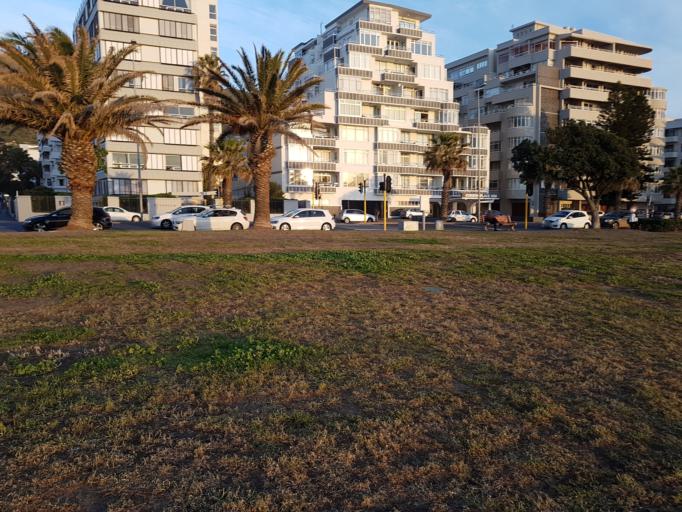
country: ZA
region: Western Cape
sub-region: City of Cape Town
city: Cape Town
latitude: -33.9107
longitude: 18.3898
